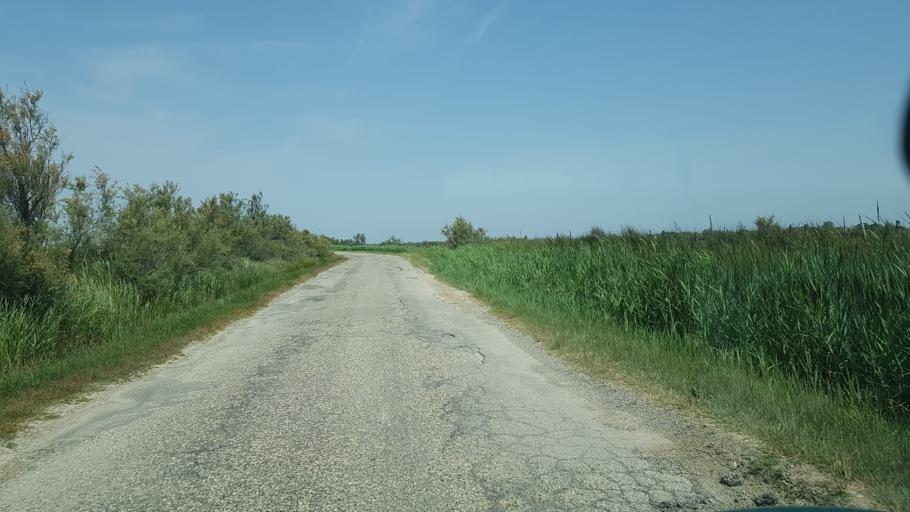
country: FR
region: Provence-Alpes-Cote d'Azur
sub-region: Departement des Bouches-du-Rhone
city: Arles
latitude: 43.5157
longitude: 4.6332
